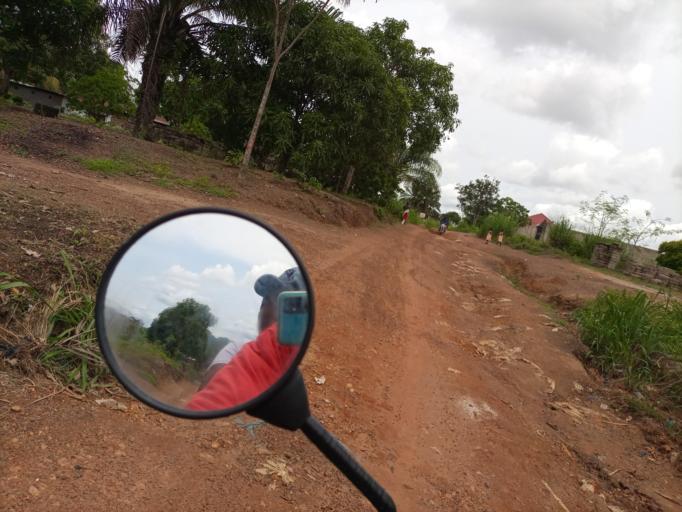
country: SL
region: Southern Province
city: Baoma
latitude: 7.9738
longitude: -11.7144
